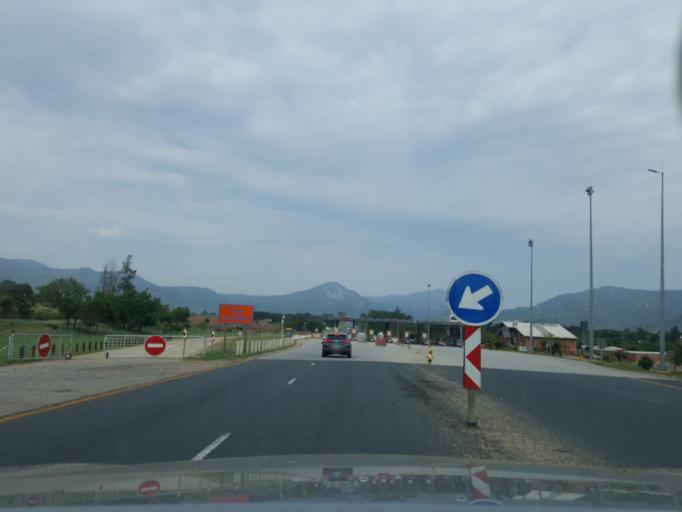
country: SZ
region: Hhohho
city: Ntfonjeni
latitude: -25.5363
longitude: 31.3466
